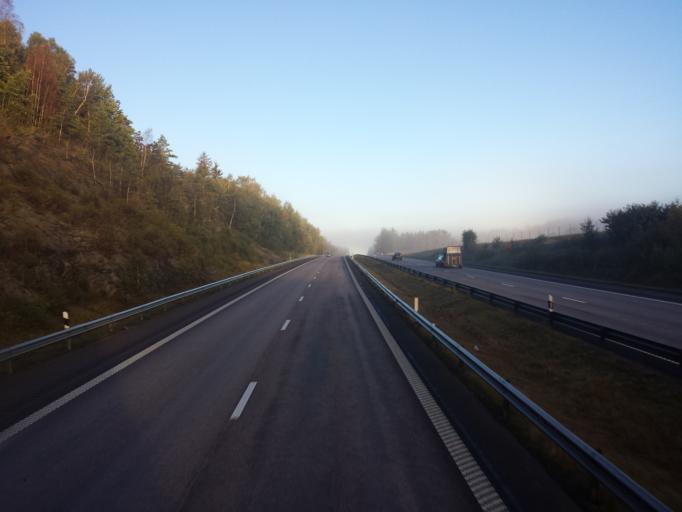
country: SE
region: Halland
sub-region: Kungsbacka Kommun
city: Fjaeras kyrkby
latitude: 57.4407
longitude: 12.1197
